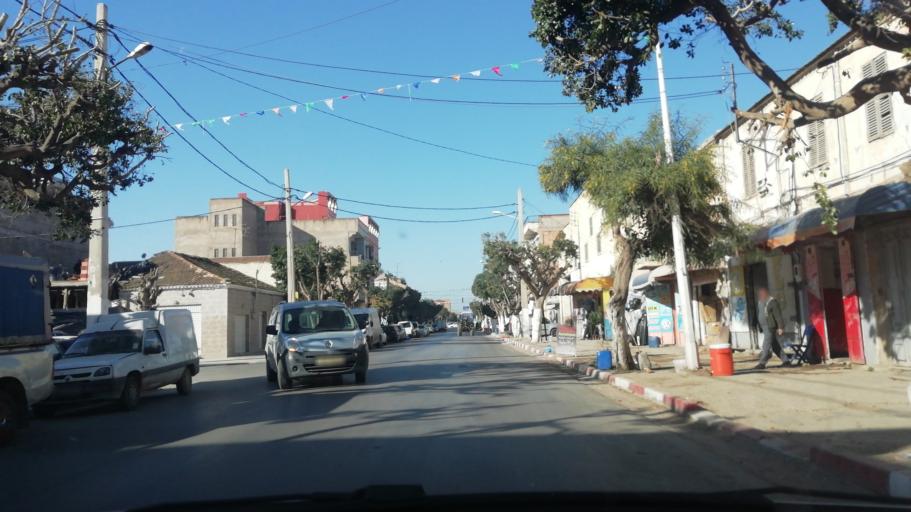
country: DZ
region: Mascara
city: Mascara
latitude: 35.5925
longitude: 0.0672
